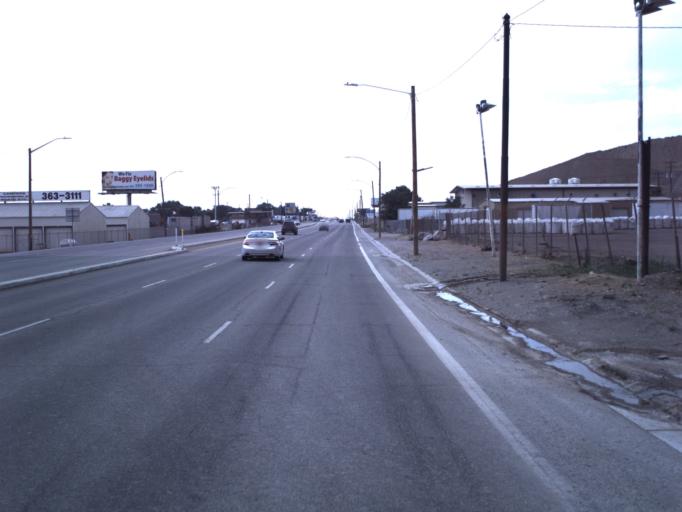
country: US
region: Utah
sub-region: Salt Lake County
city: Salt Lake City
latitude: 40.7970
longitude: -111.9067
